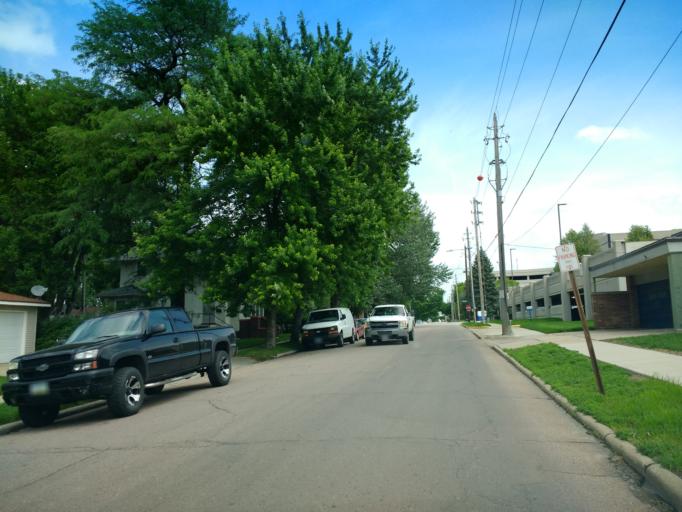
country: US
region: Iowa
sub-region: Woodbury County
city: Sioux City
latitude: 42.5207
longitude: -96.4065
